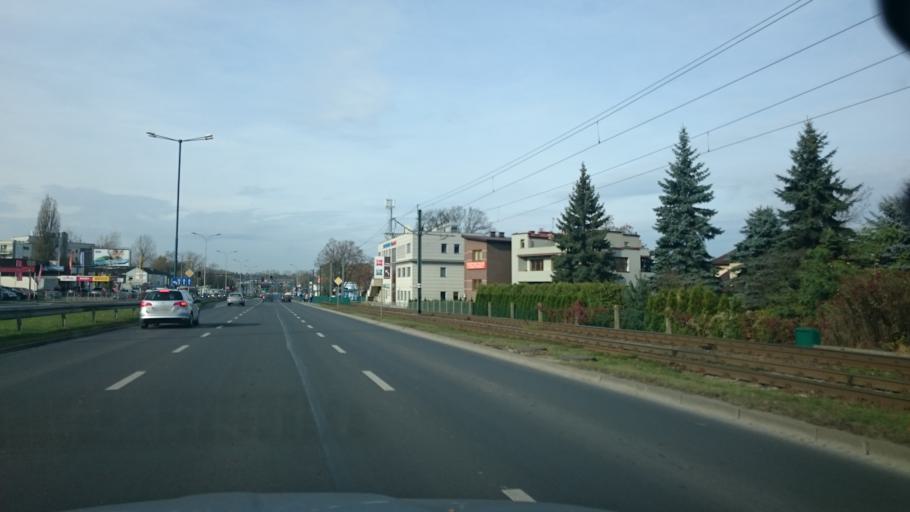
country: PL
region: Lesser Poland Voivodeship
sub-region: Krakow
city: Krakow
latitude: 50.0221
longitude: 19.9832
